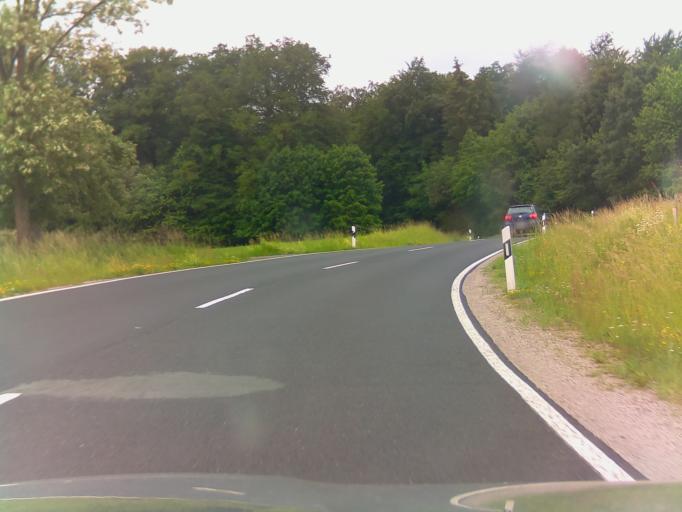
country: DE
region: Bavaria
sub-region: Regierungsbezirk Unterfranken
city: Oberleichtersbach
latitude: 50.2422
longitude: 9.8215
